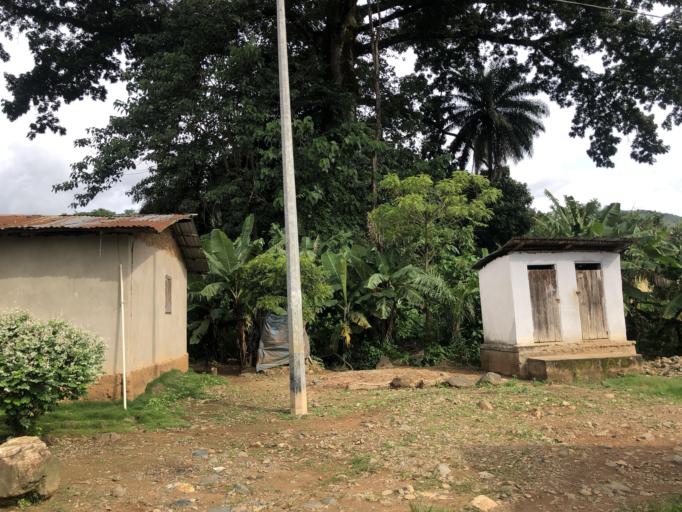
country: SL
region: Northern Province
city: Bumbuna
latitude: 9.0419
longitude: -11.7425
